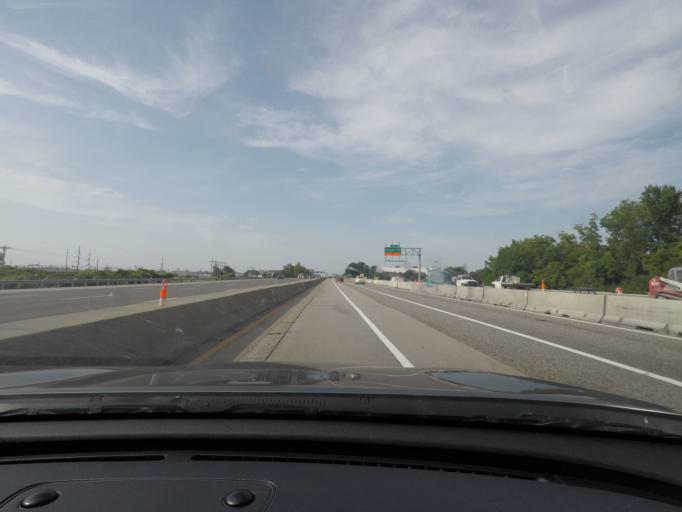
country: US
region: Missouri
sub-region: Saint Louis County
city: Maryland Heights
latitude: 38.7257
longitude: -90.4449
